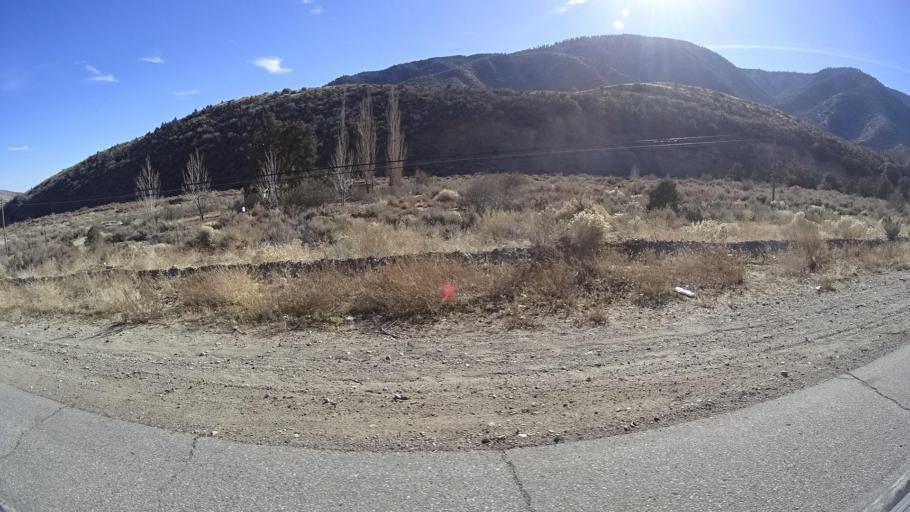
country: US
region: California
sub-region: Kern County
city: Frazier Park
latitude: 34.8212
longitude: -118.9291
